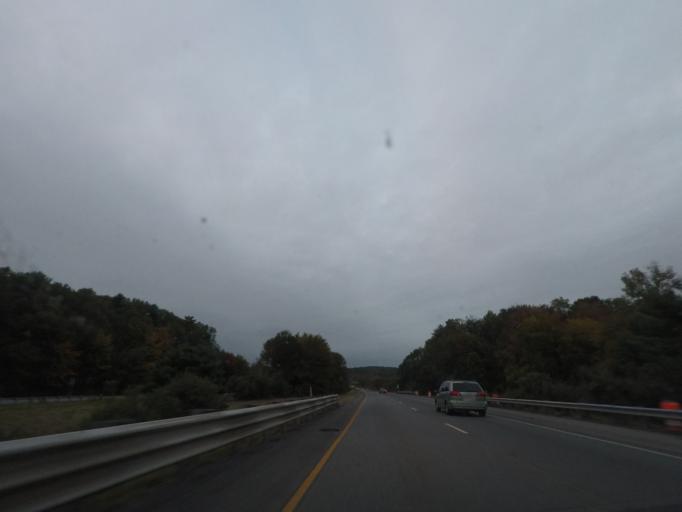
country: US
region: Massachusetts
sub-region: Worcester County
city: Oxford
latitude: 42.1066
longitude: -71.8556
